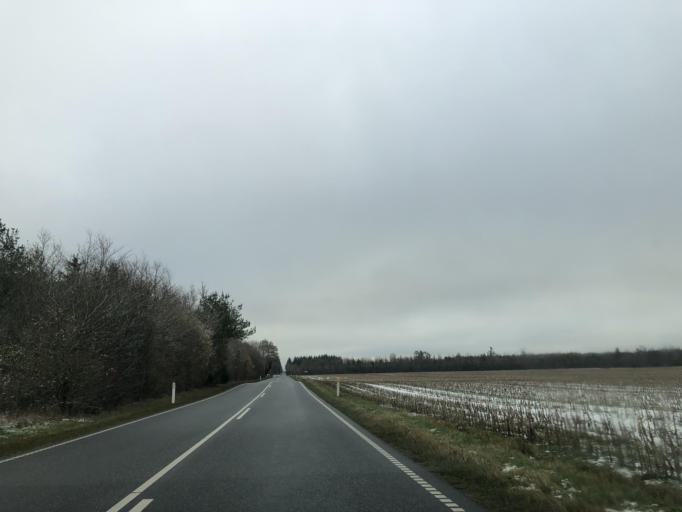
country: DK
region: Central Jutland
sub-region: Ikast-Brande Kommune
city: Brande
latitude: 55.9877
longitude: 9.2284
